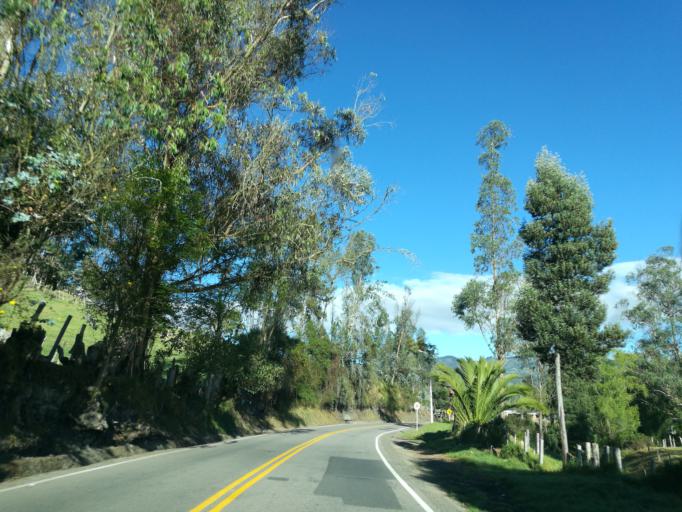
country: CO
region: Boyaca
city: Chiquinquira
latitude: 5.6281
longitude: -73.7914
